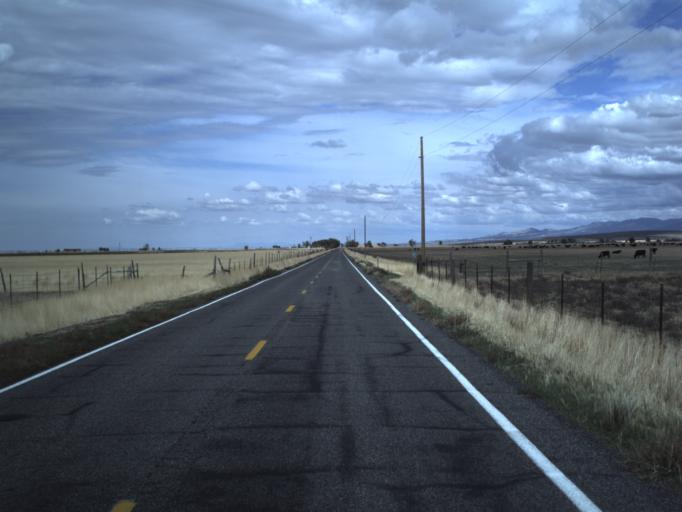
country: US
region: Utah
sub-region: Millard County
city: Fillmore
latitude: 39.0264
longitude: -112.4100
